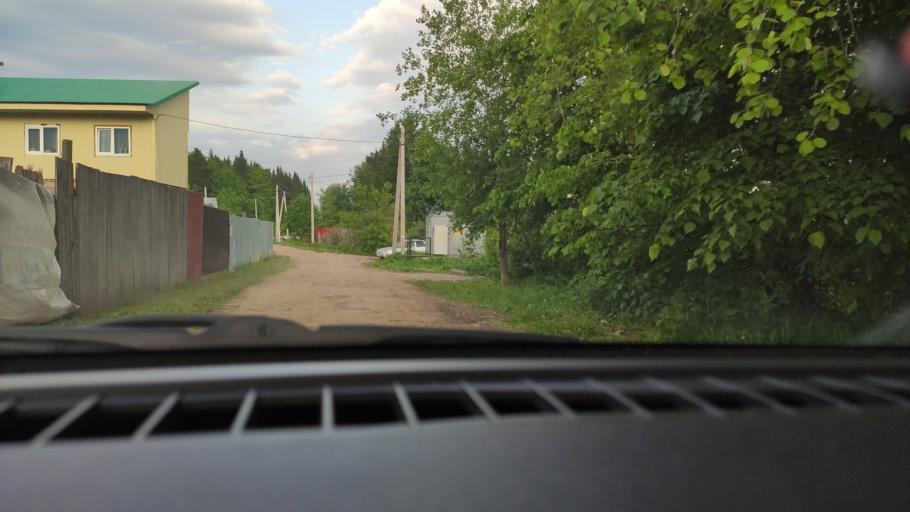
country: RU
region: Perm
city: Froly
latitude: 57.9502
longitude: 56.2829
